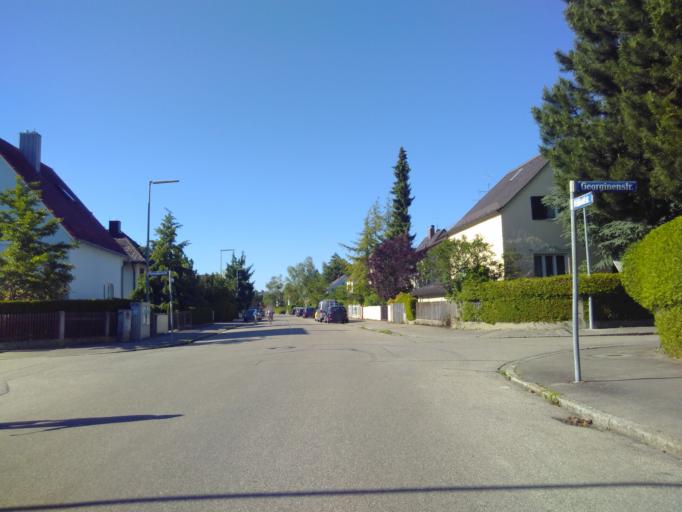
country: DE
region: Bavaria
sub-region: Upper Bavaria
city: Pasing
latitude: 48.1272
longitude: 11.4833
